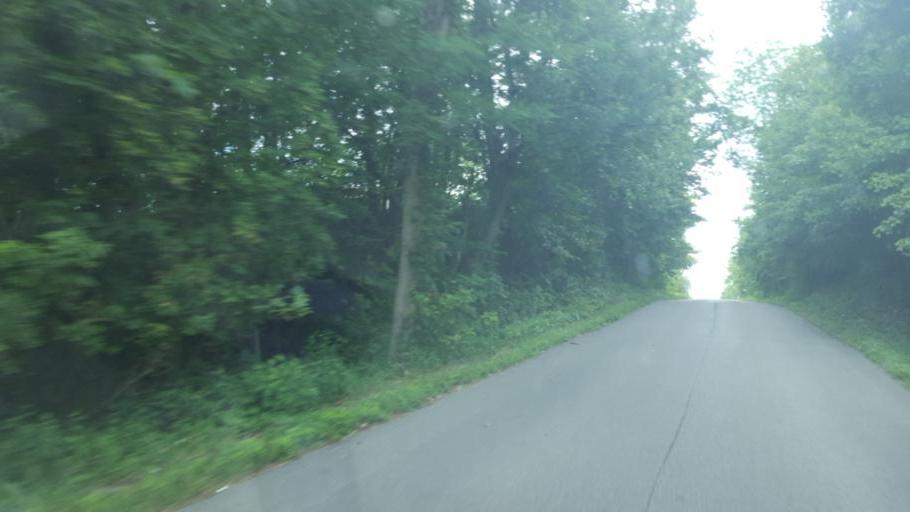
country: US
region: Ohio
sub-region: Morrow County
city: Cardington
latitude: 40.3933
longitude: -82.8068
